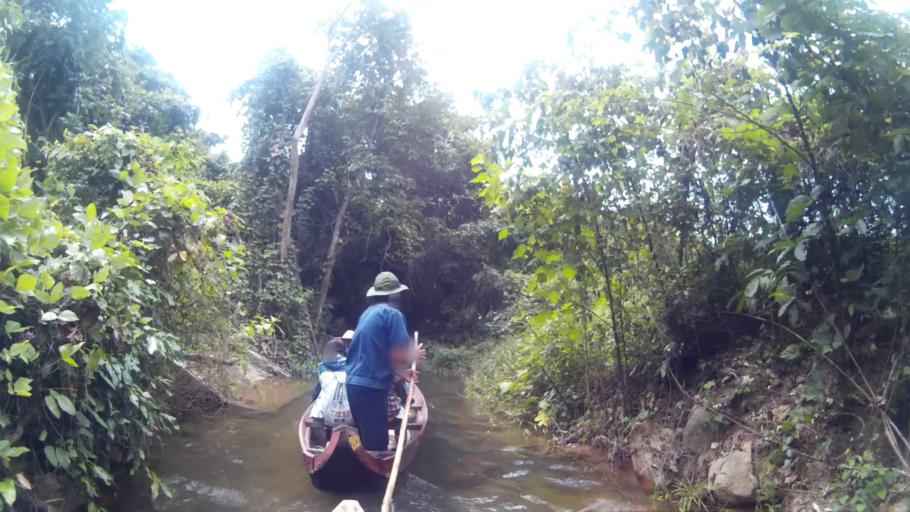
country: VN
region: Binh Dinh
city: Phu Phong
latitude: 13.8748
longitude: 108.8644
